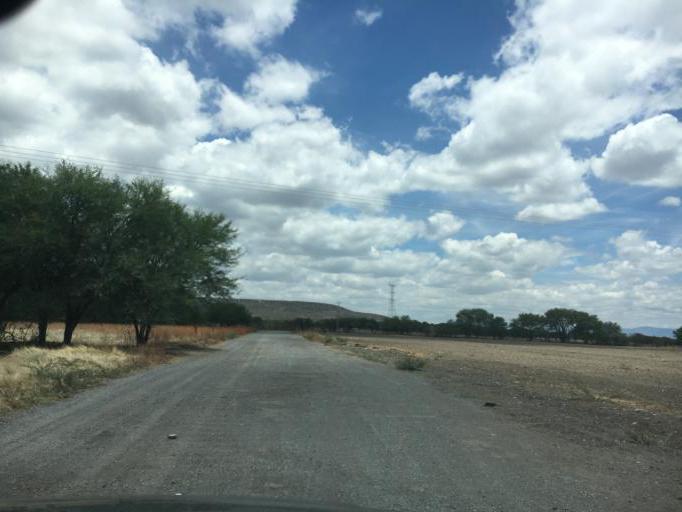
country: MX
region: Guanajuato
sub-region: Leon
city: Plan Guanajuato (La Sandia)
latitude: 20.9173
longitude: -101.7485
